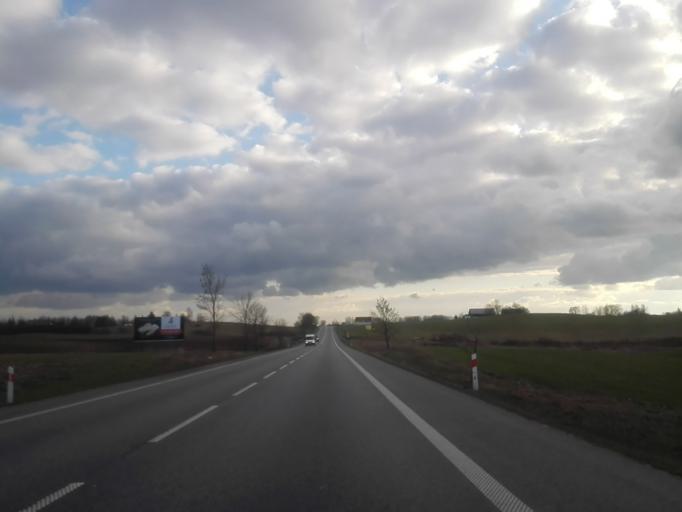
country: PL
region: Podlasie
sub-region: Suwalki
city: Suwalki
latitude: 54.2063
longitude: 23.0245
